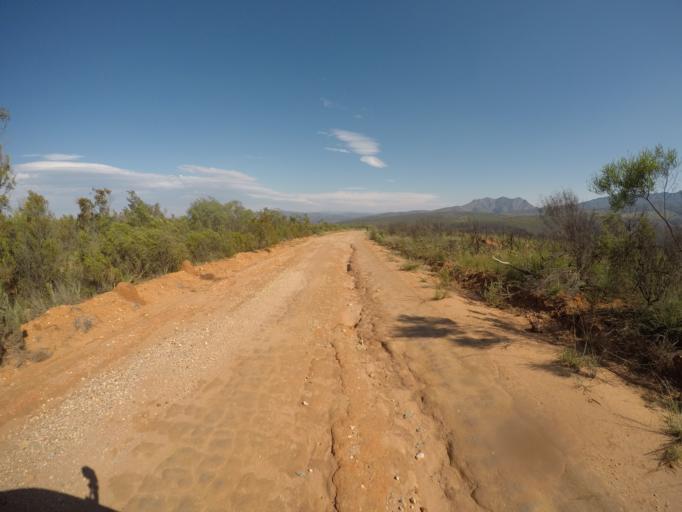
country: ZA
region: Eastern Cape
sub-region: Cacadu District Municipality
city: Kareedouw
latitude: -33.6365
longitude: 24.4575
